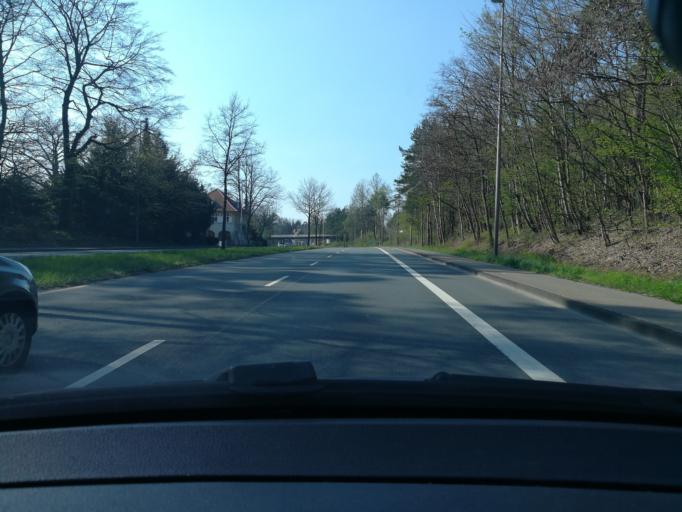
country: DE
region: North Rhine-Westphalia
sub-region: Regierungsbezirk Detmold
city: Bielefeld
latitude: 51.9798
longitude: 8.5323
